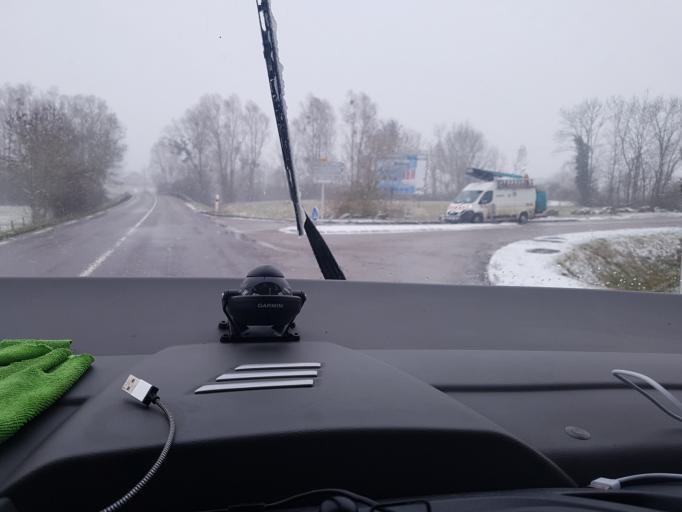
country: FR
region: Lorraine
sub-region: Departement de la Moselle
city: Remilly
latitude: 48.8823
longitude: 6.3987
